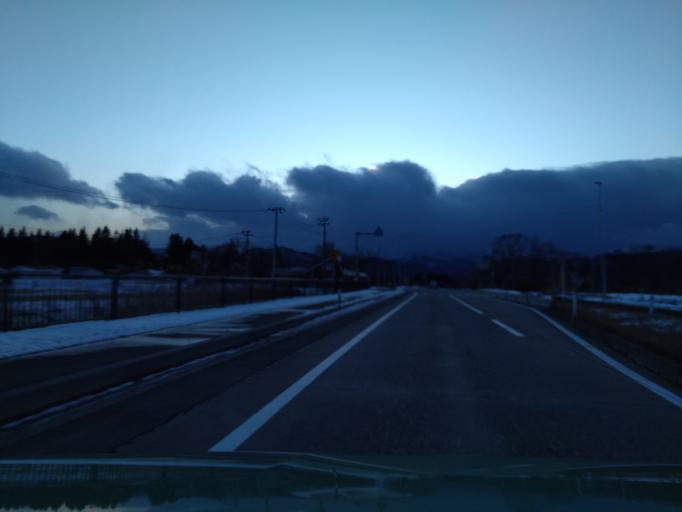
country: JP
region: Iwate
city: Shizukuishi
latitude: 39.7005
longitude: 140.9589
